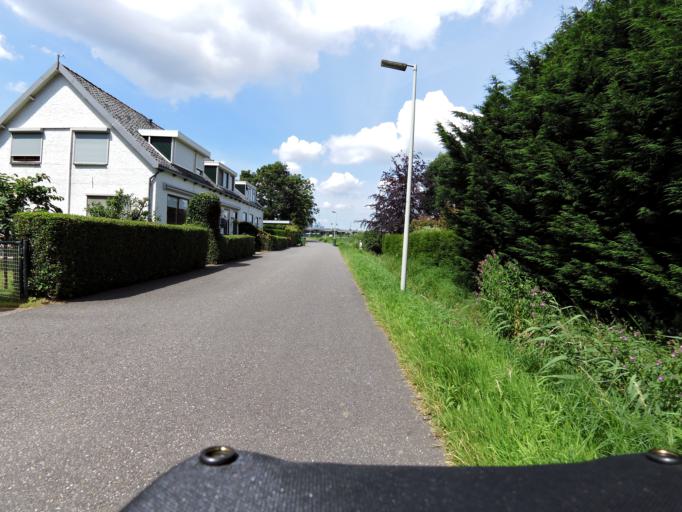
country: NL
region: South Holland
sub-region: Gemeente Albrandswaard
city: Rhoon
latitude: 51.8660
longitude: 4.4321
